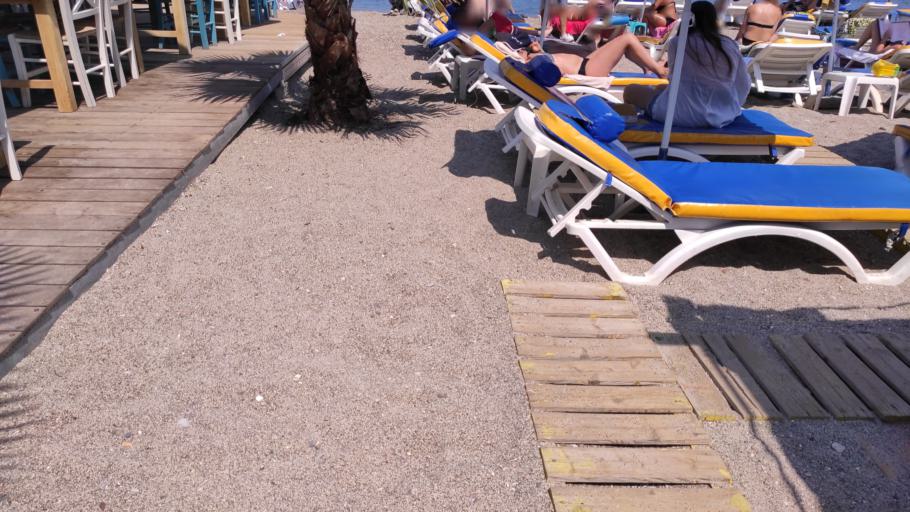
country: GR
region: South Aegean
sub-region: Nomos Dodekanisou
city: Kos
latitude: 36.8991
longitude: 27.2862
